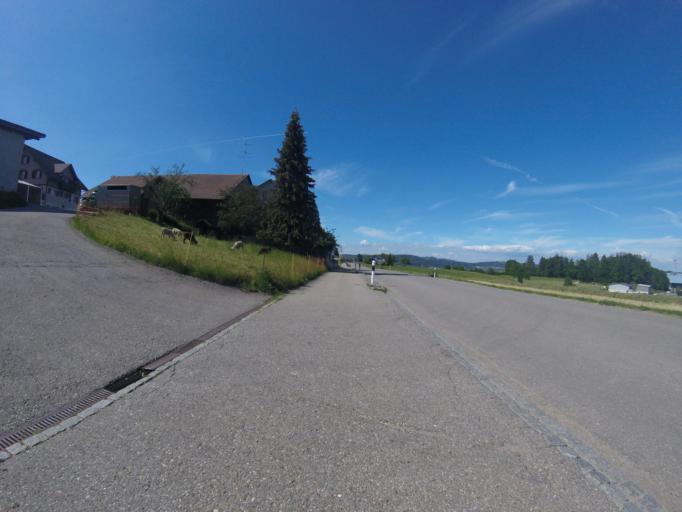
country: CH
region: Saint Gallen
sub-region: Wahlkreis Toggenburg
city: Kirchberg
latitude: 47.4215
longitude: 9.0623
